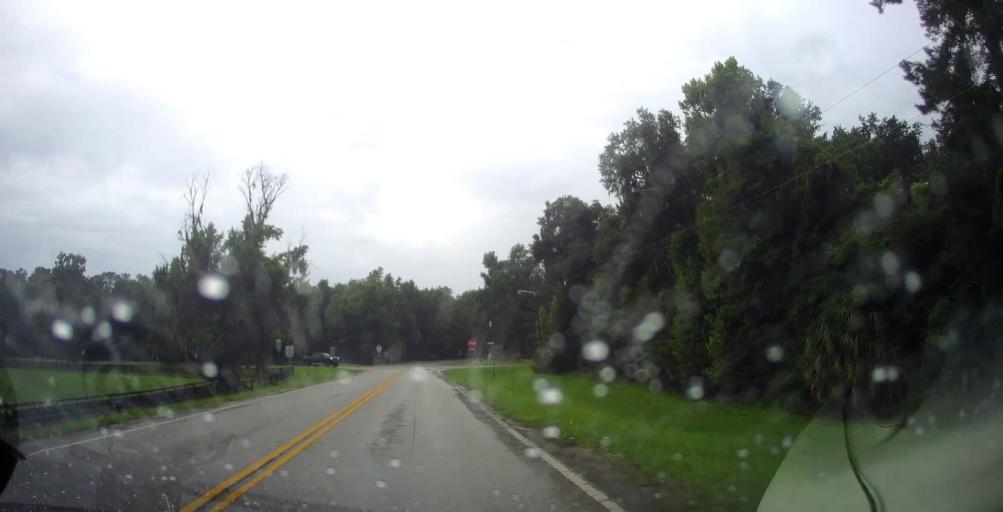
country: US
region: Florida
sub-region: Marion County
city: Citra
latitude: 29.3618
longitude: -82.2515
